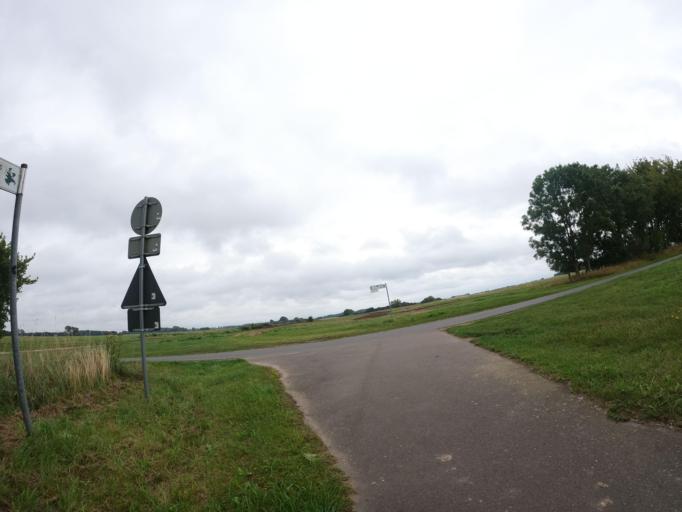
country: DE
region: Mecklenburg-Vorpommern
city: Poseritz
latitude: 54.2835
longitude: 13.2619
